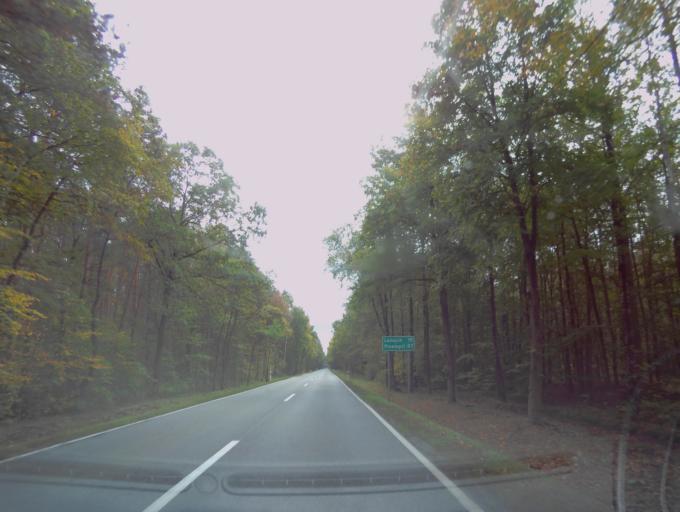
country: PL
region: Subcarpathian Voivodeship
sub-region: Powiat nizanski
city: Krzeszow
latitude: 50.3970
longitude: 22.2975
